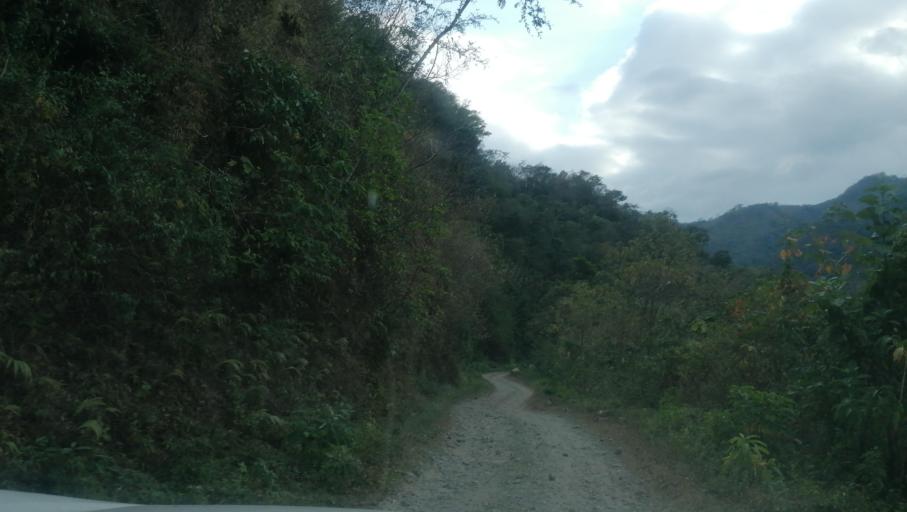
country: MX
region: Chiapas
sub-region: Cacahoatan
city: Benito Juarez
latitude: 15.1591
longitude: -92.1775
